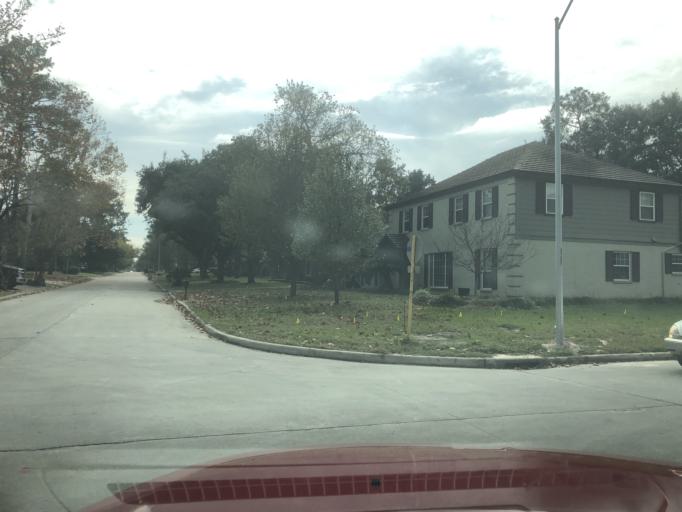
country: US
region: Texas
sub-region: Harris County
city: Spring
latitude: 30.0219
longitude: -95.4635
